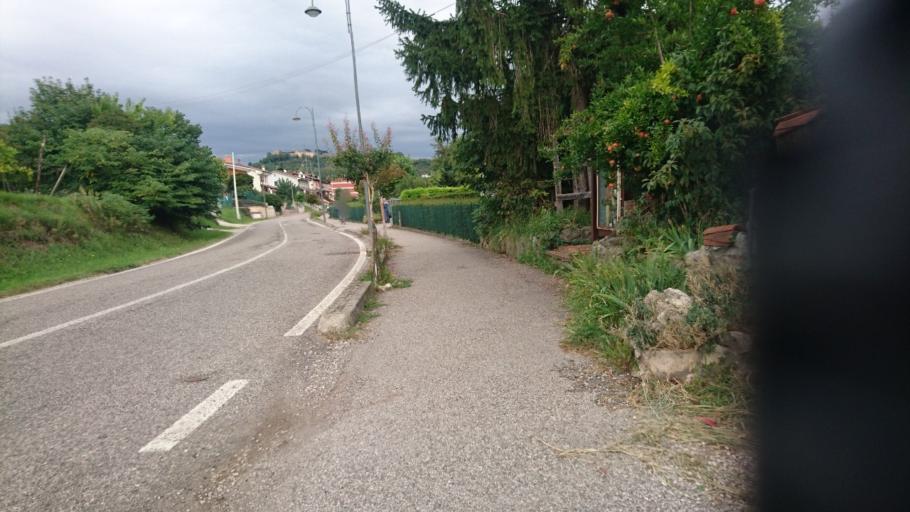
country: IT
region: Veneto
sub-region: Provincia di Vicenza
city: Montebello Vicentino
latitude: 45.4537
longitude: 11.3751
